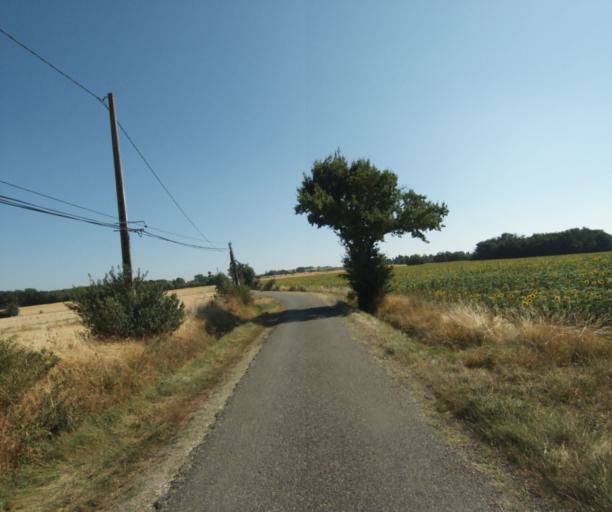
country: FR
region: Midi-Pyrenees
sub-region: Departement de la Haute-Garonne
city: Saint-Felix-Lauragais
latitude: 43.4905
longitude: 1.9217
